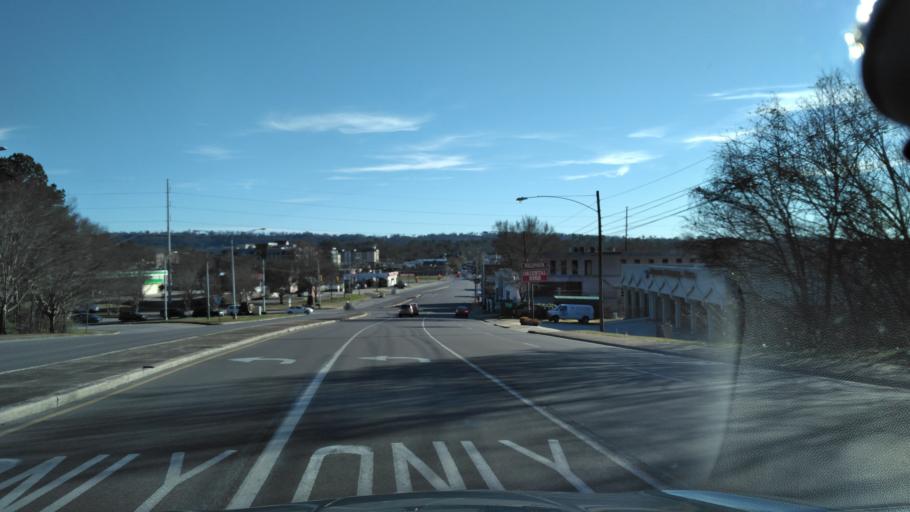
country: US
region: Alabama
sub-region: Jefferson County
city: Homewood
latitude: 33.4852
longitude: -86.7920
